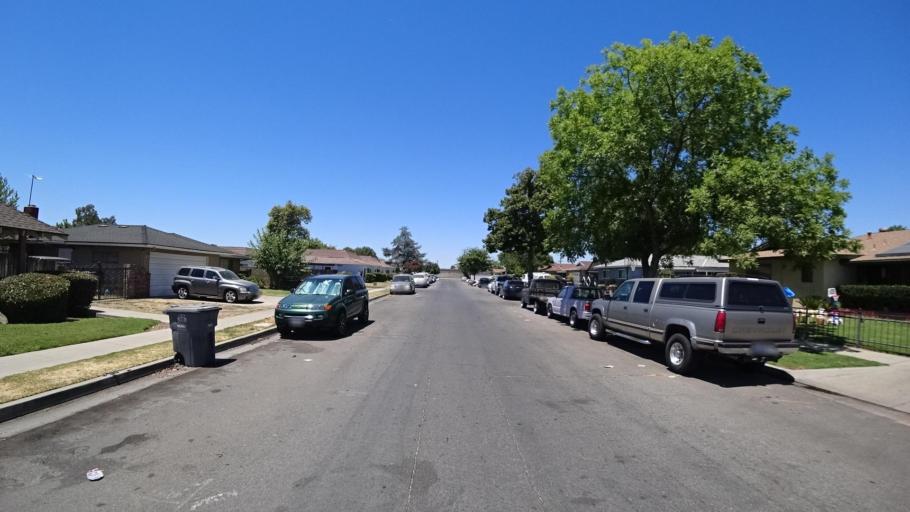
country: US
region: California
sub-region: Fresno County
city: Fresno
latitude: 36.7813
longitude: -119.7466
